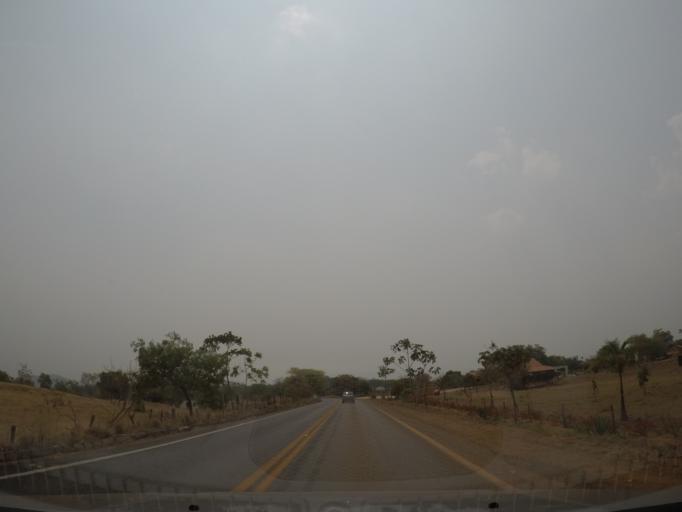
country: BR
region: Goias
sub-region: Pirenopolis
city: Pirenopolis
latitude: -15.8844
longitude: -48.9017
